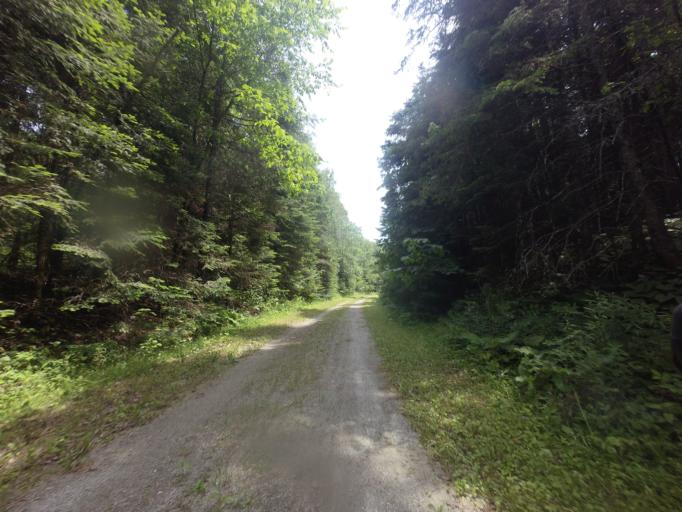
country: CA
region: Quebec
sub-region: Outaouais
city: Wakefield
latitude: 45.8576
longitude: -75.9927
